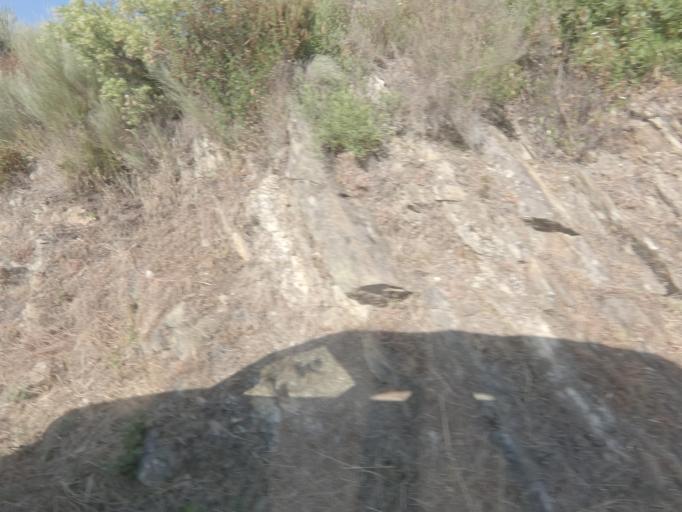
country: PT
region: Vila Real
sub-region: Sabrosa
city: Sabrosa
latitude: 41.2335
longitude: -7.5239
